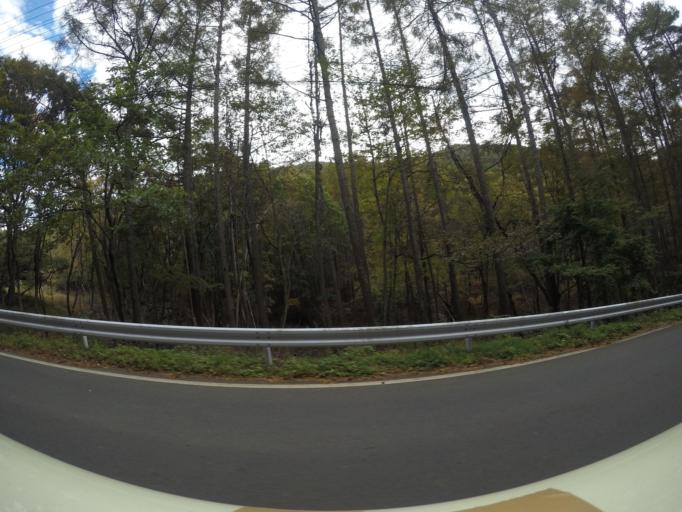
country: JP
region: Nagano
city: Chino
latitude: 35.9601
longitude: 138.1129
